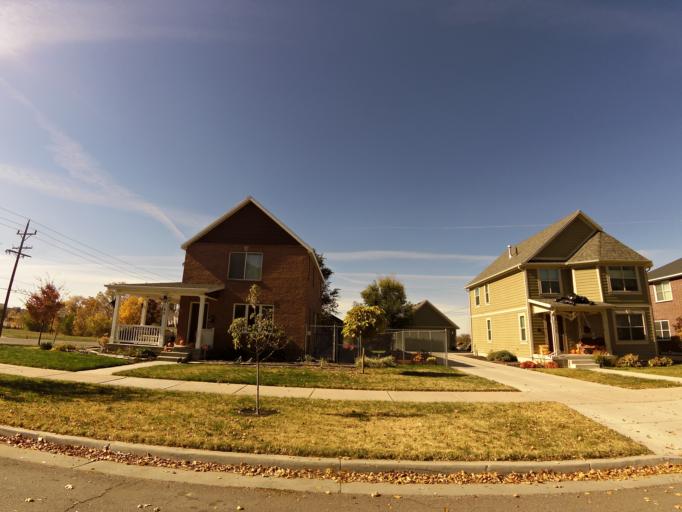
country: US
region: Utah
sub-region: Weber County
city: Ogden
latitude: 41.2272
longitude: -111.9648
